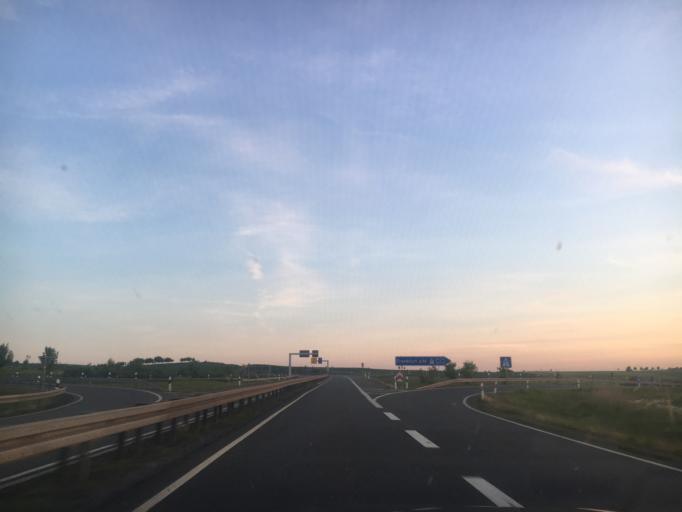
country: DE
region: Thuringia
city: Schwaara
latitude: 50.9047
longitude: 12.1292
